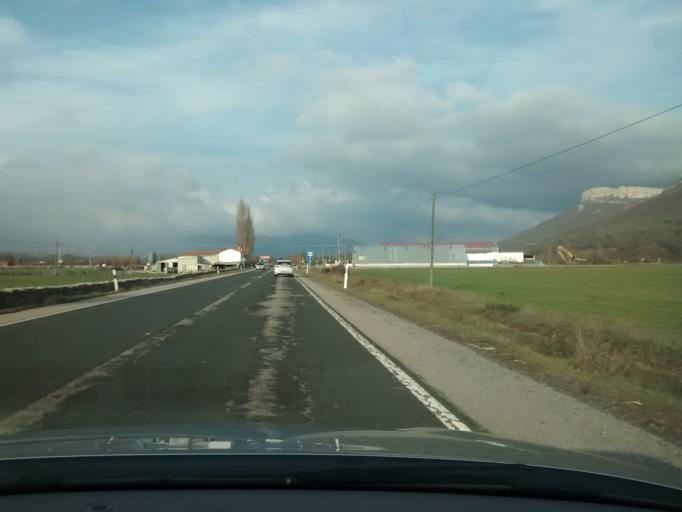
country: ES
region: Castille and Leon
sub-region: Provincia de Burgos
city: Espinosa de los Monteros
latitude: 43.0553
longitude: -3.4805
